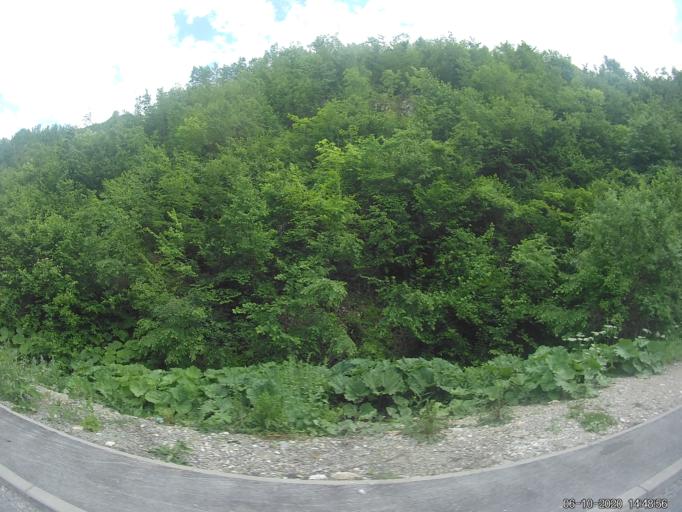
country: XK
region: Prizren
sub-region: Komuna e Therandes
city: Budakovo
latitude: 42.3928
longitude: 20.9660
